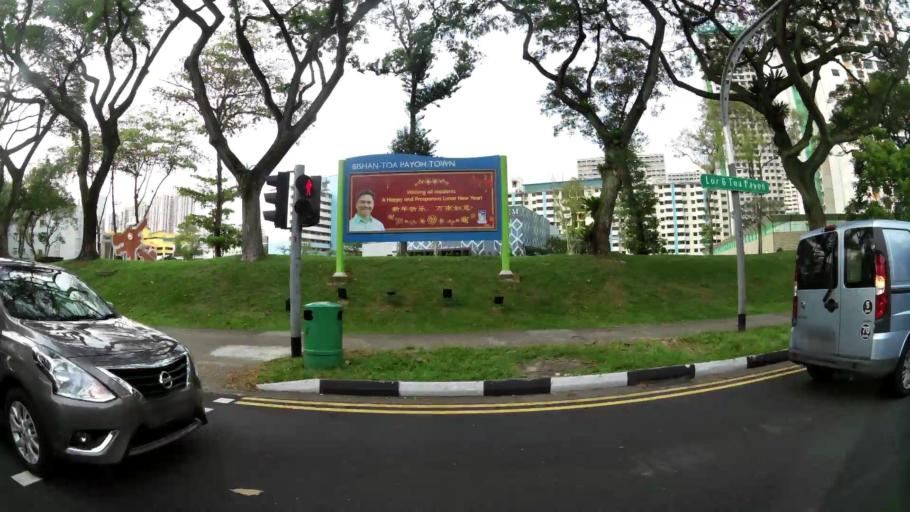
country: SG
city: Singapore
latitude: 1.3318
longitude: 103.8548
